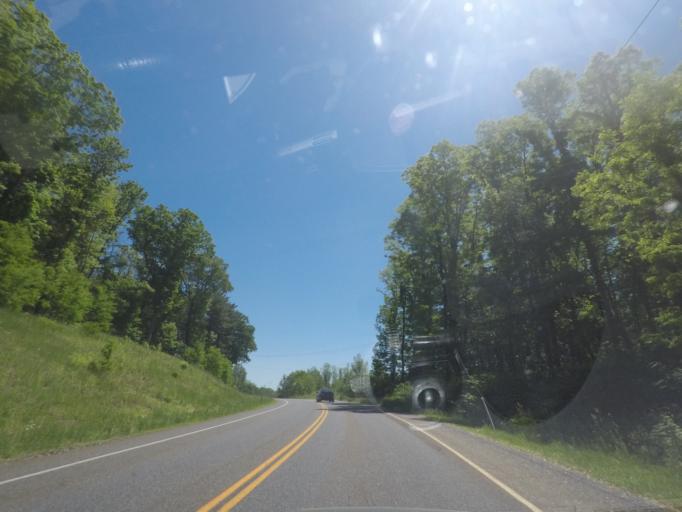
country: US
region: New York
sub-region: Saratoga County
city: Mechanicville
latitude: 42.9469
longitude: -73.7203
